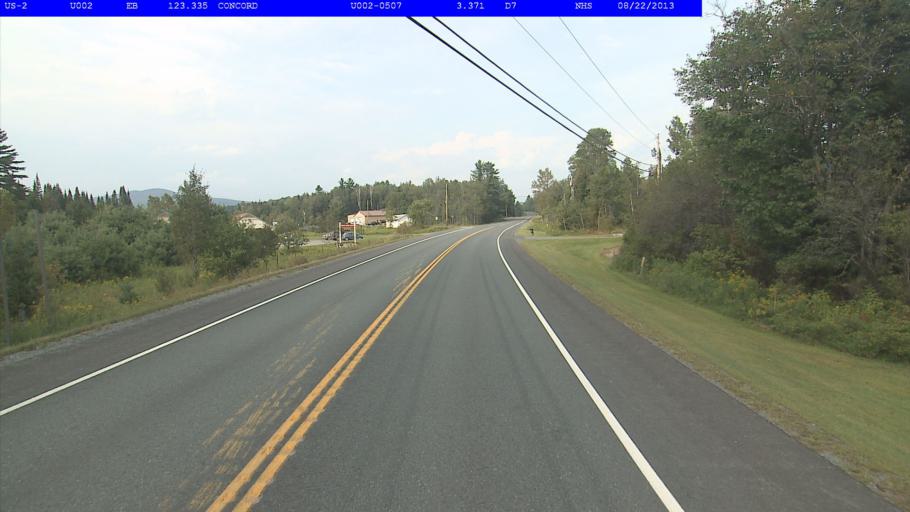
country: US
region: Vermont
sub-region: Caledonia County
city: St Johnsbury
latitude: 44.4428
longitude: -71.8780
